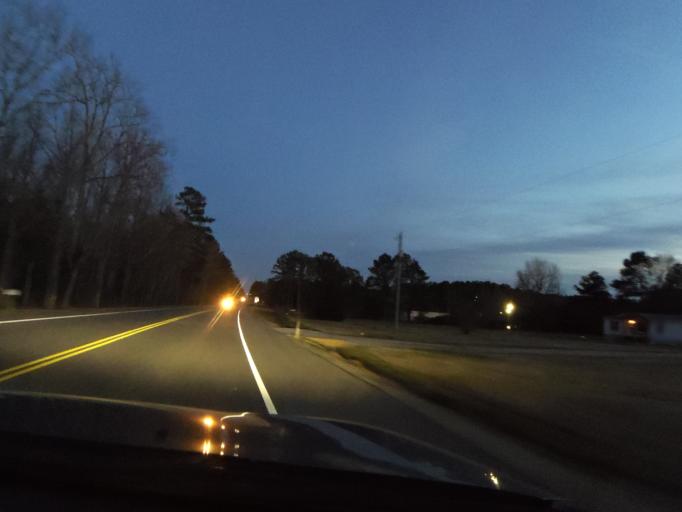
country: US
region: Virginia
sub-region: City of Petersburg
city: Petersburg
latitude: 37.0853
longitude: -77.3639
